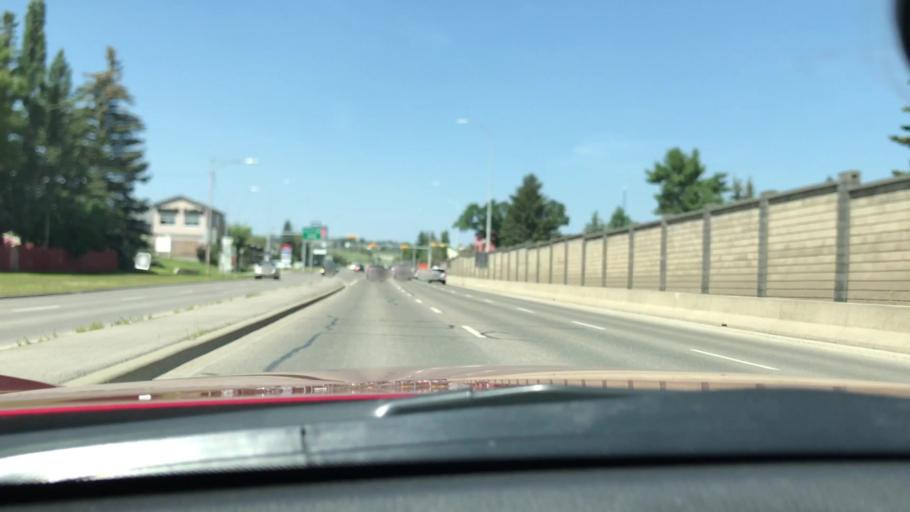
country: CA
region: Alberta
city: Calgary
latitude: 51.0481
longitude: -114.1506
